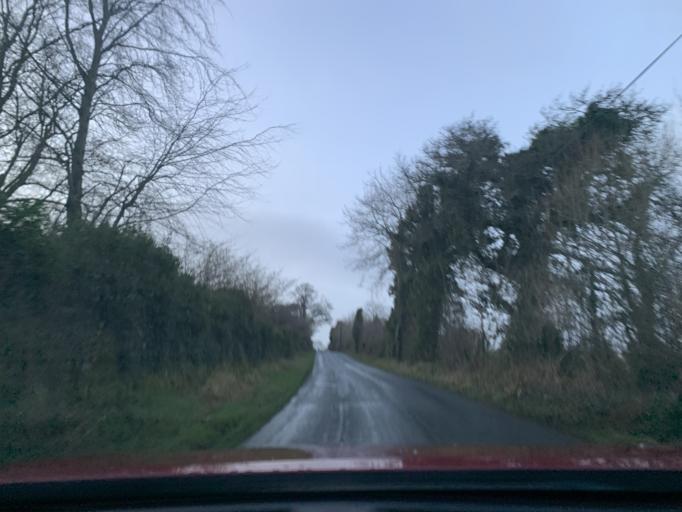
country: IE
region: Connaught
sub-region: Sligo
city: Ballymote
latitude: 54.1186
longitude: -8.5765
